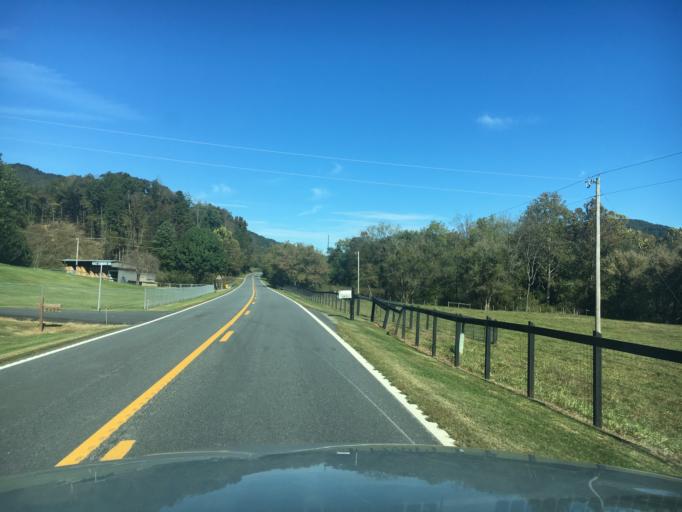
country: US
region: North Carolina
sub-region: Rutherford County
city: Spindale
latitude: 35.5251
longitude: -81.8554
